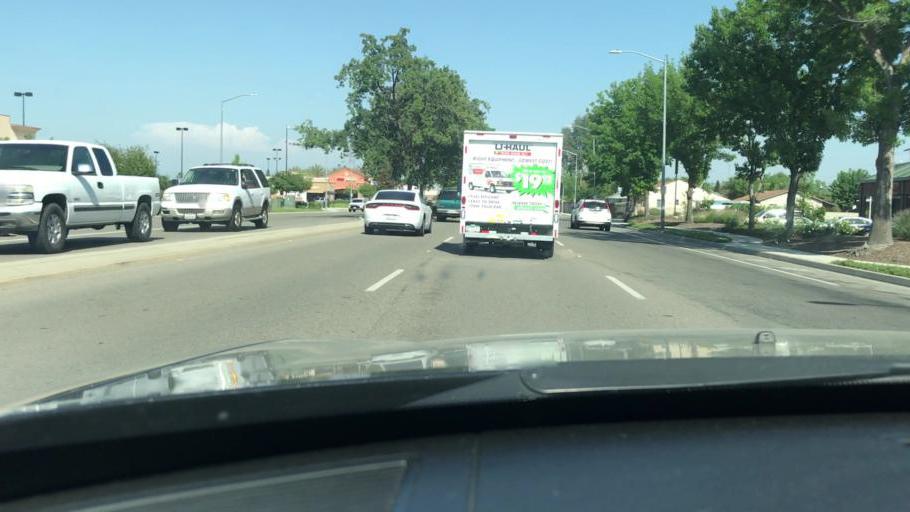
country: US
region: California
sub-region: Fresno County
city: Clovis
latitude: 36.8374
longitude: -119.6972
